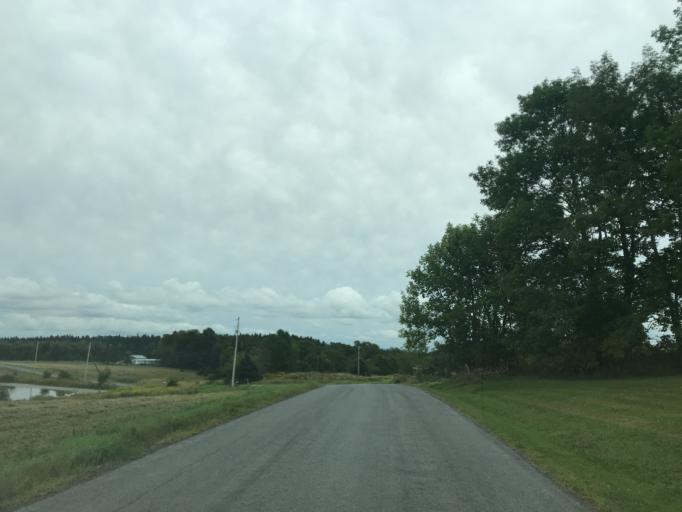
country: US
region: New York
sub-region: Otsego County
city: Worcester
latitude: 42.5378
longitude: -74.6464
